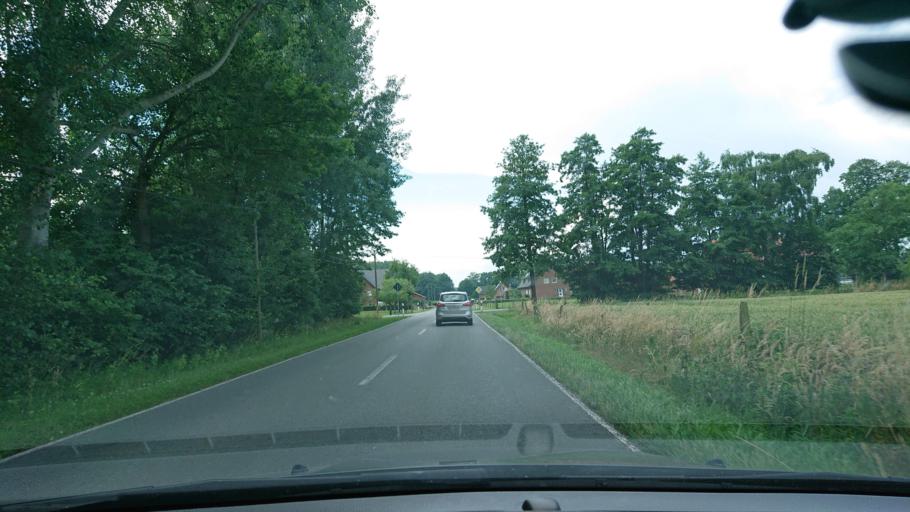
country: DE
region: North Rhine-Westphalia
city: Rietberg
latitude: 51.7937
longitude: 8.4088
